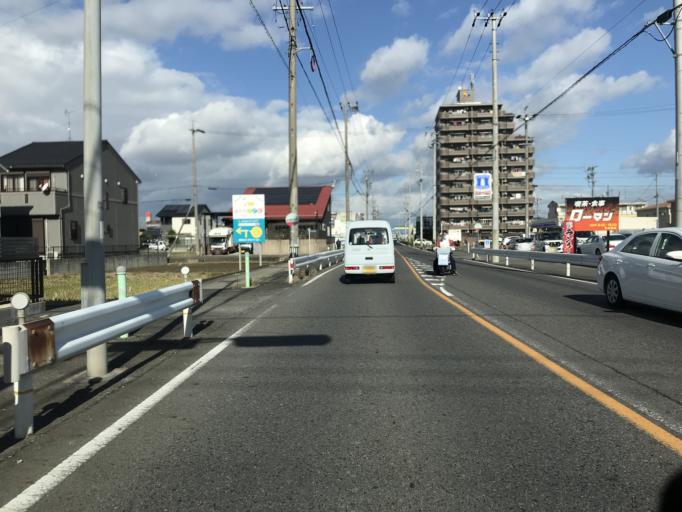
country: JP
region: Aichi
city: Komaki
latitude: 35.2455
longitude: 136.8952
